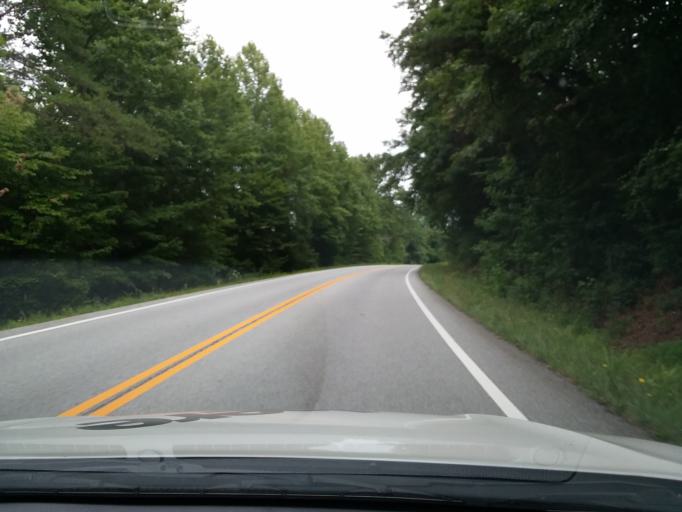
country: US
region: Georgia
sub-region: Rabun County
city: Clayton
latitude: 34.8255
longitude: -83.3219
